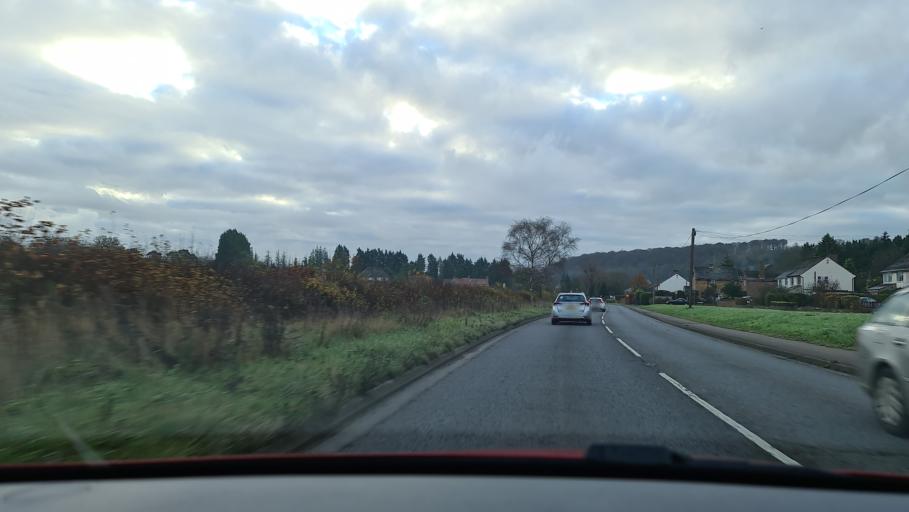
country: GB
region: England
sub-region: Buckinghamshire
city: Princes Risborough
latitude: 51.6780
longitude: -0.8253
